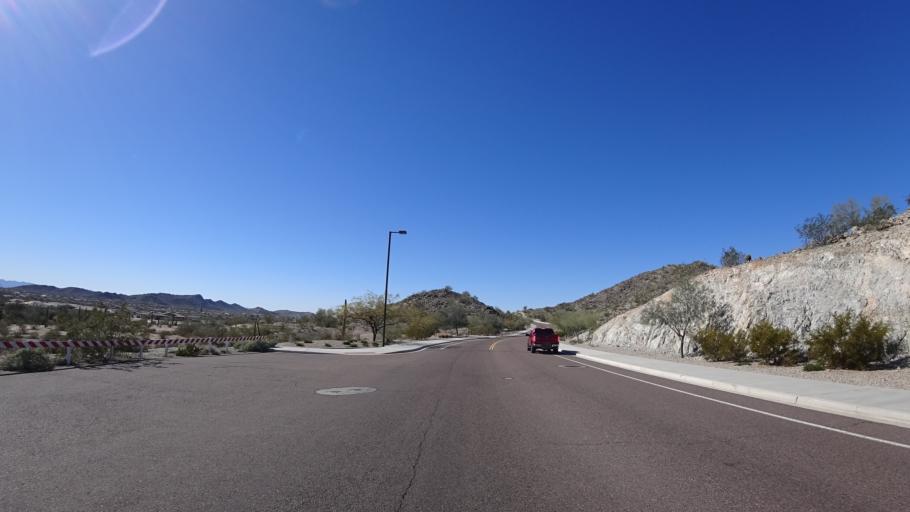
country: US
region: Arizona
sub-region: Maricopa County
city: Goodyear
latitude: 33.3405
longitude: -112.4408
